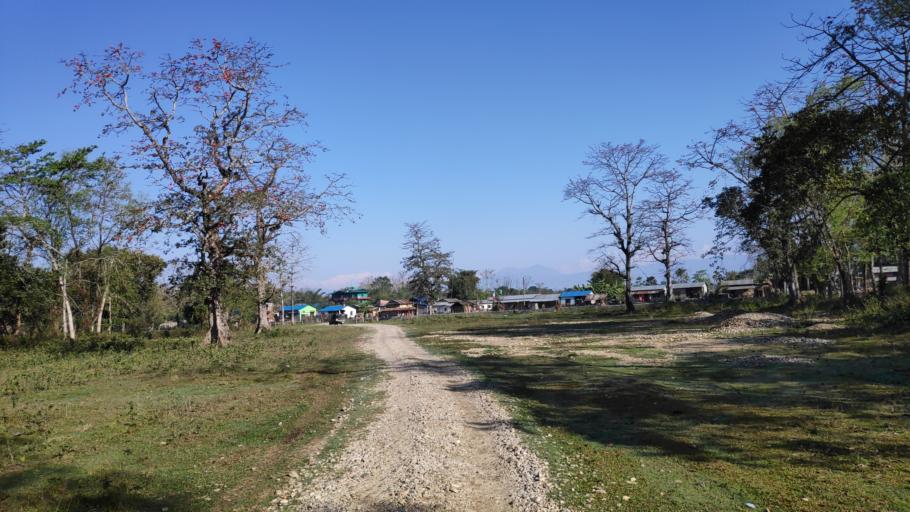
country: NP
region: Central Region
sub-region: Narayani Zone
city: Bharatpur
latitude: 27.5657
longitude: 84.5221
